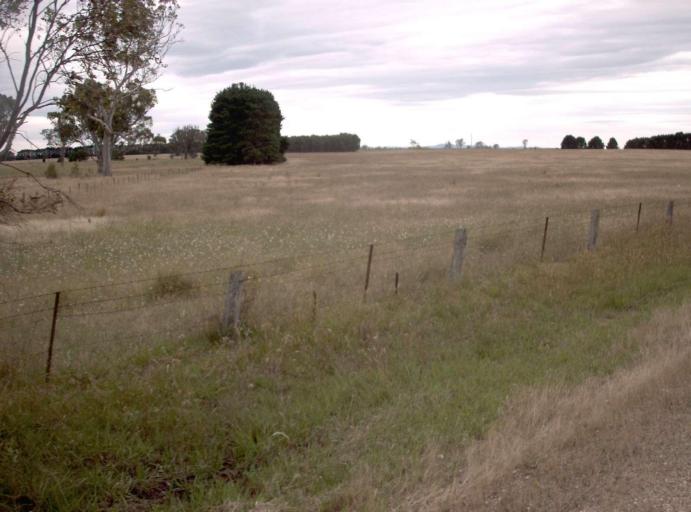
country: AU
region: Victoria
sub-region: East Gippsland
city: Bairnsdale
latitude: -37.9680
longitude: 147.4801
